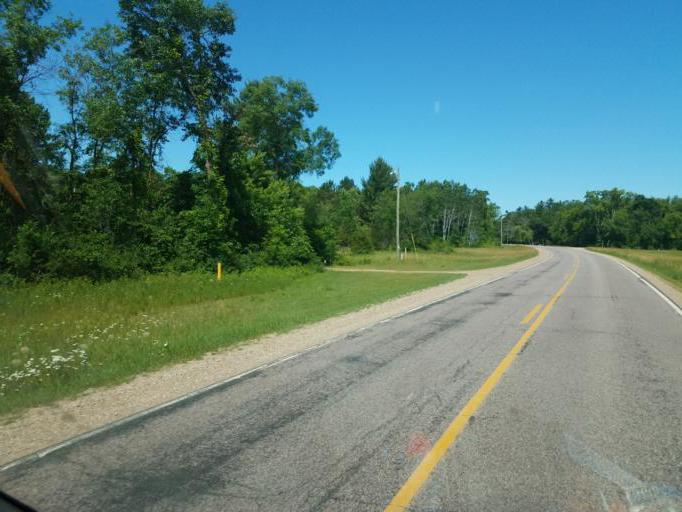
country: US
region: Wisconsin
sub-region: Adams County
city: Adams
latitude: 43.8124
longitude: -89.8904
